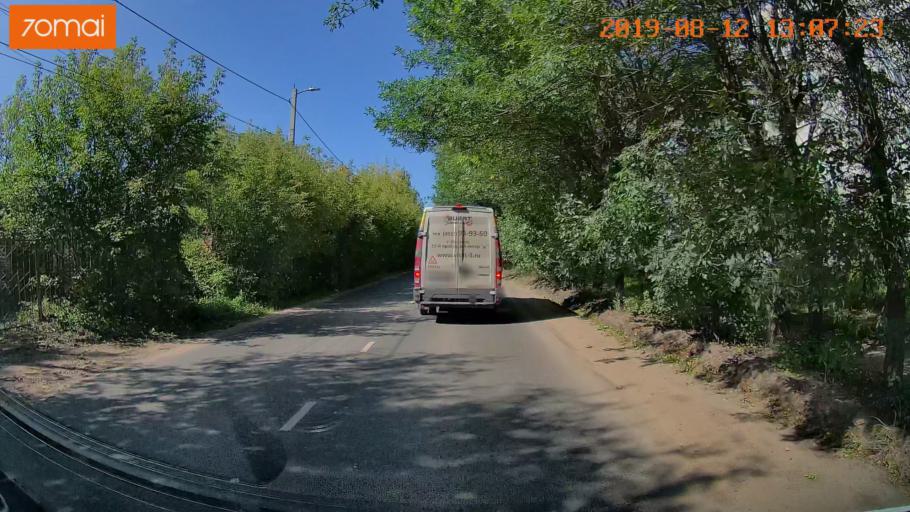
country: RU
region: Ivanovo
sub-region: Gorod Ivanovo
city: Ivanovo
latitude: 57.0070
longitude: 41.0009
